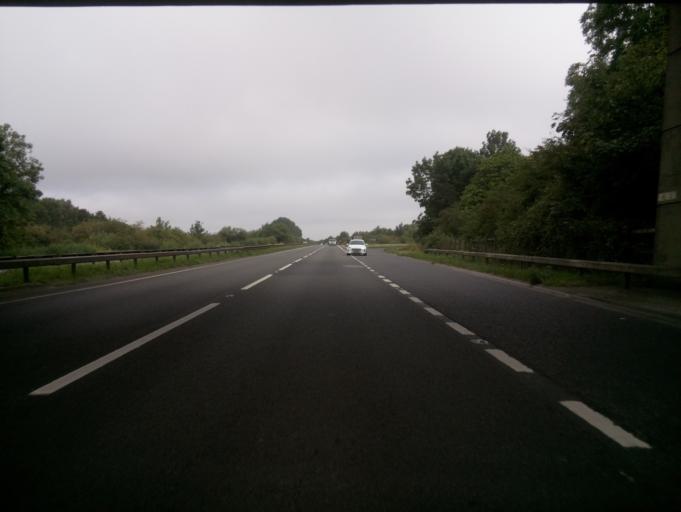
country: GB
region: England
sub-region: Wiltshire
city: Cricklade
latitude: 51.6411
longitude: -1.8431
